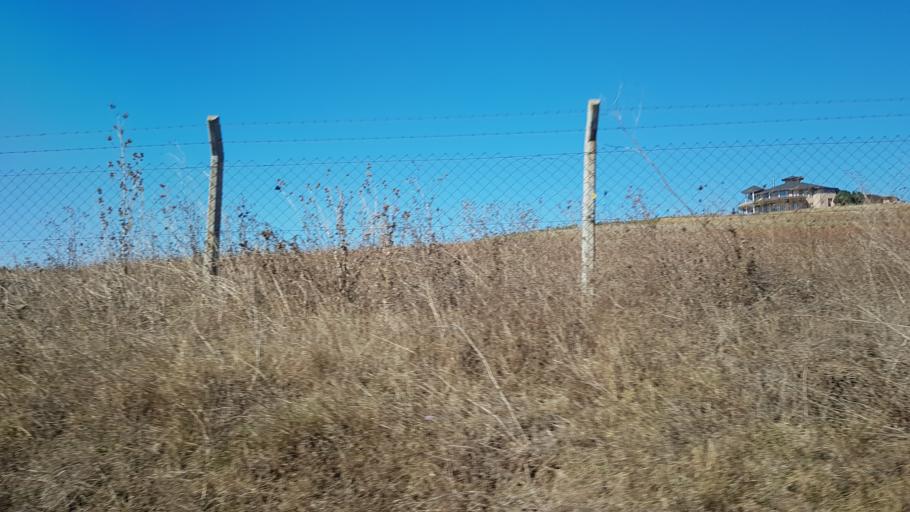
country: TR
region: Tekirdag
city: Corlu
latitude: 41.0380
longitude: 27.8144
